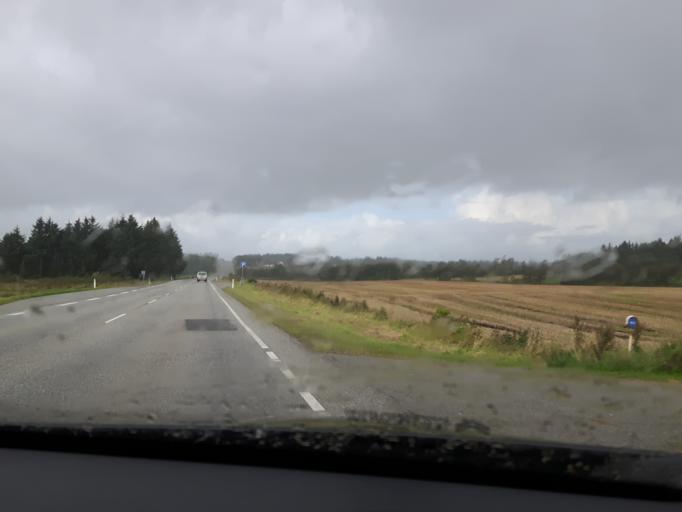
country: DK
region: North Denmark
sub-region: Jammerbugt Kommune
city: Fjerritslev
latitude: 57.0879
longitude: 9.3260
